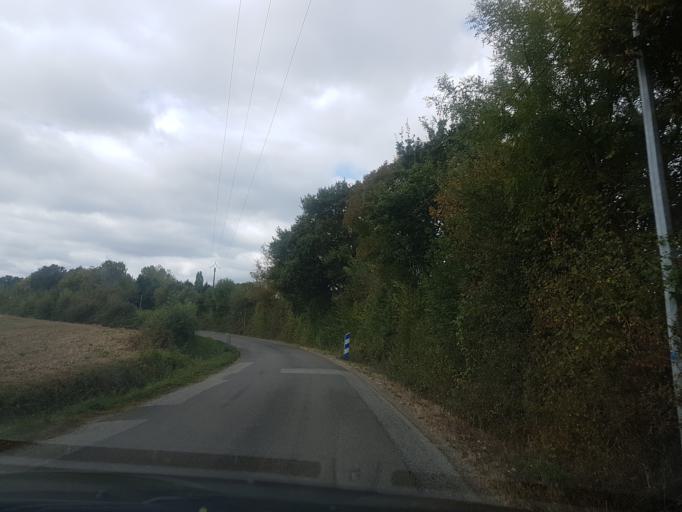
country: FR
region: Pays de la Loire
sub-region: Departement de la Loire-Atlantique
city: Ligne
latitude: 47.4047
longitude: -1.3897
